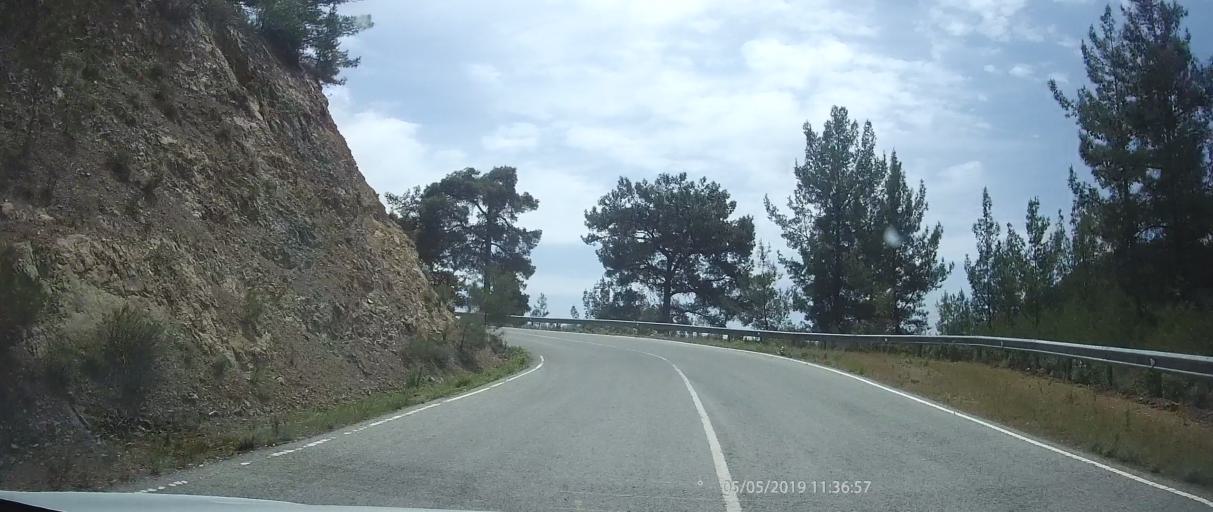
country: CY
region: Lefkosia
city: Kato Pyrgos
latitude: 34.9717
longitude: 32.6556
